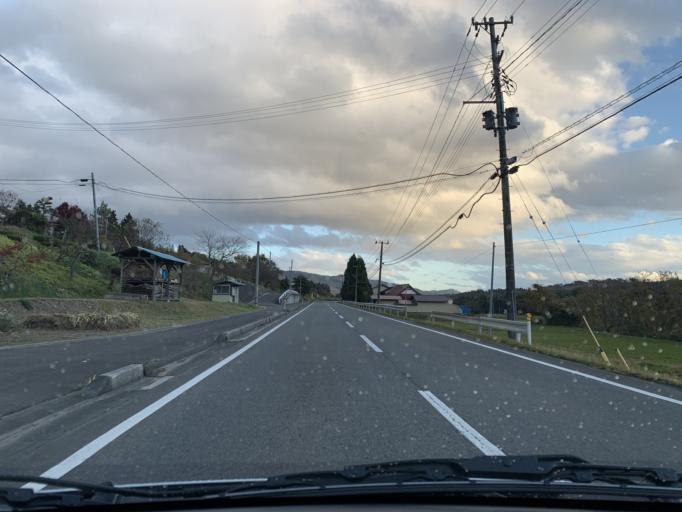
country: JP
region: Iwate
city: Mizusawa
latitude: 39.0510
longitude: 141.0935
